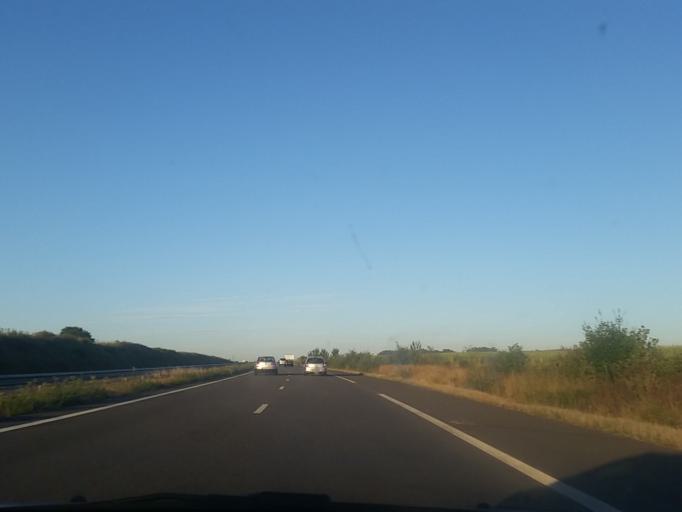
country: FR
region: Pays de la Loire
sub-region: Departement de la Loire-Atlantique
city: Le Pellerin
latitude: 47.1837
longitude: -1.7626
